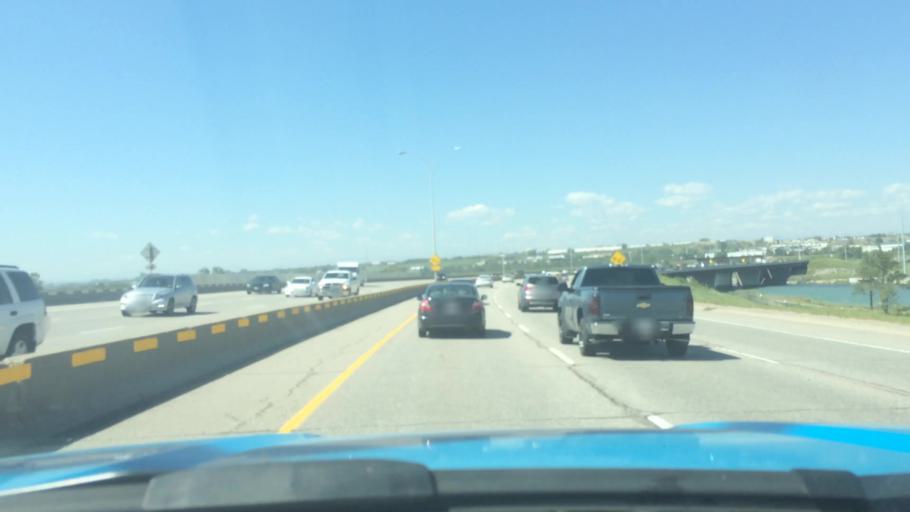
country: CA
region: Alberta
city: Calgary
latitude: 51.0093
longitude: -114.0129
